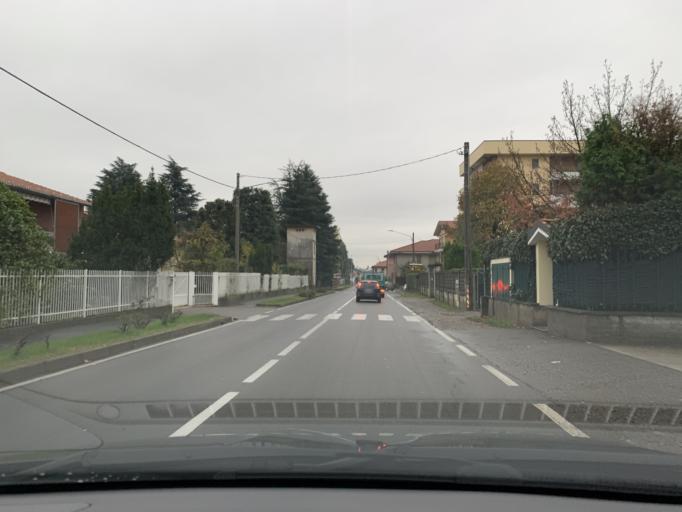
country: IT
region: Lombardy
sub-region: Provincia di Como
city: Rovello Porro
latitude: 45.6413
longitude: 9.0473
